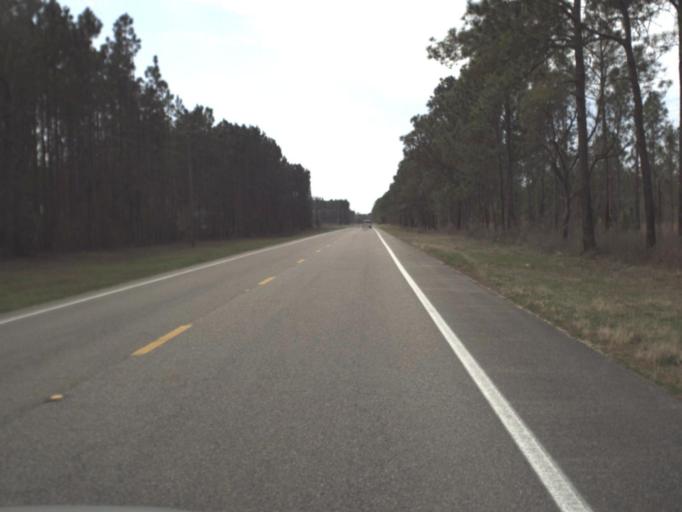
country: US
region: Florida
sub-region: Liberty County
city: Bristol
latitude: 30.4624
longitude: -84.9519
